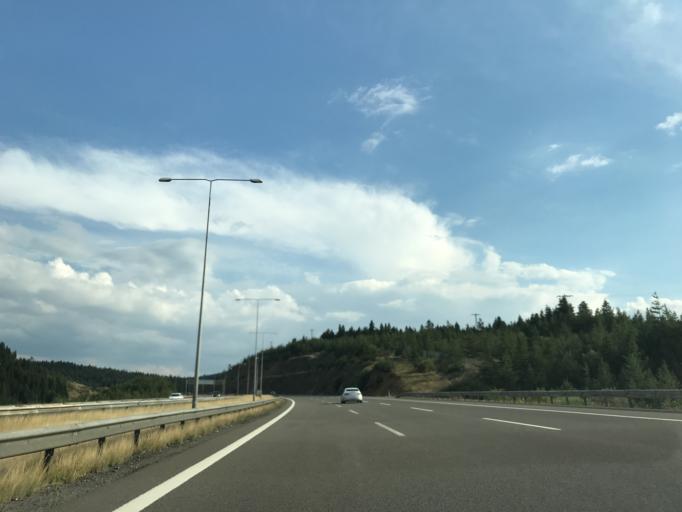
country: TR
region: Ankara
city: Pecenek
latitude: 40.5873
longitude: 32.2867
